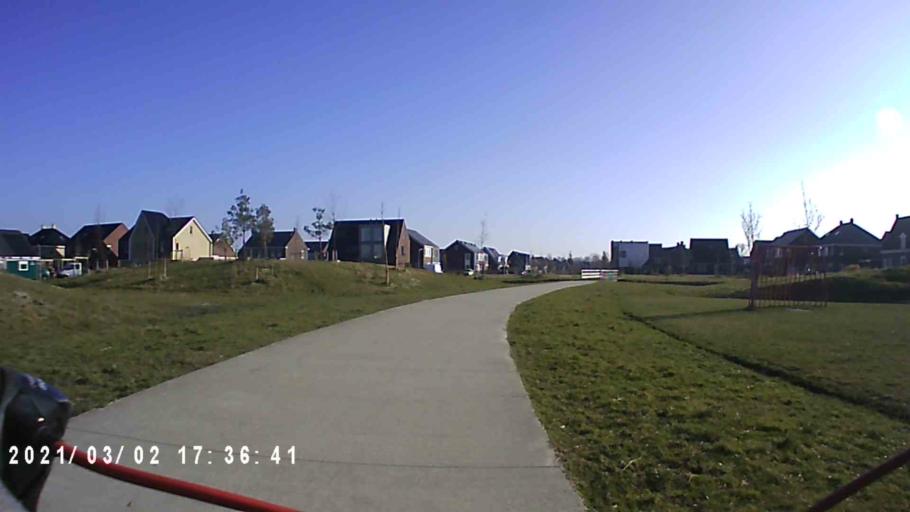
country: NL
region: Groningen
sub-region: Gemeente Zuidhorn
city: Zuidhorn
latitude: 53.2513
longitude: 6.4130
